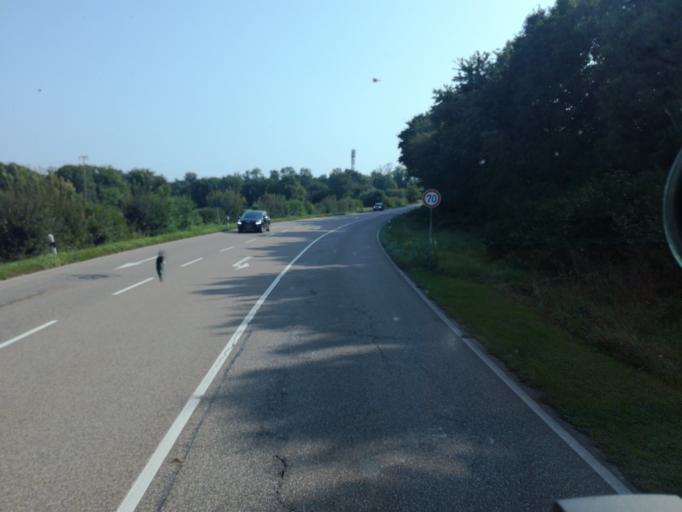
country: DE
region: Baden-Wuerttemberg
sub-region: Karlsruhe Region
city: Rheinau
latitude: 48.8758
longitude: 8.1878
